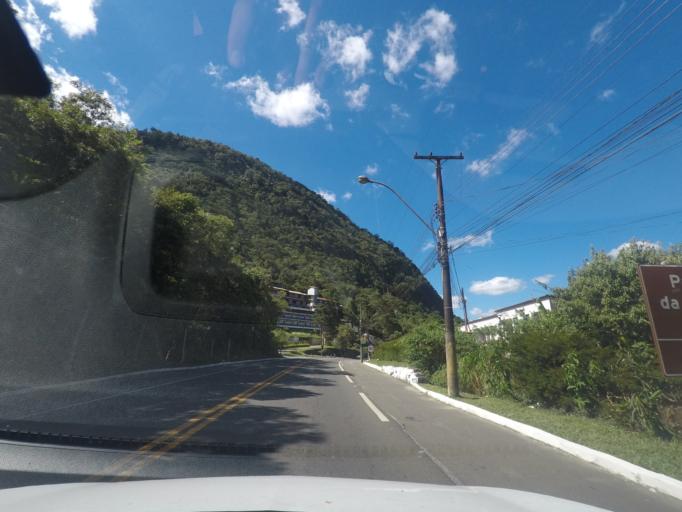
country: BR
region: Rio de Janeiro
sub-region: Teresopolis
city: Teresopolis
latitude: -22.4611
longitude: -42.9879
